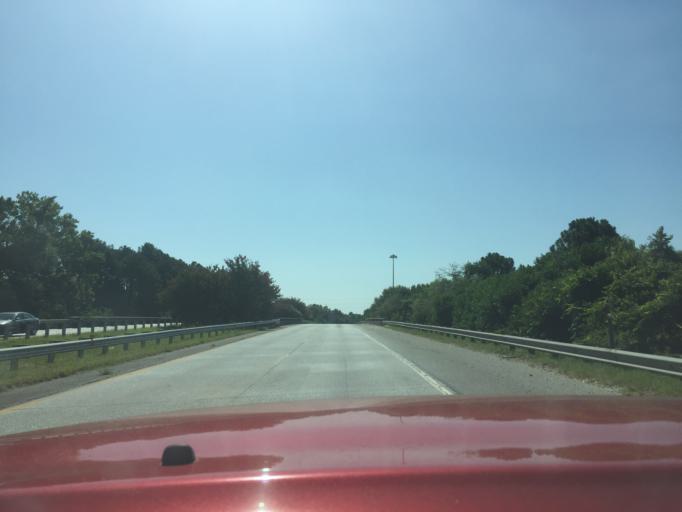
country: US
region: Georgia
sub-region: Chatham County
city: Garden City
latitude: 32.0929
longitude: -81.1324
